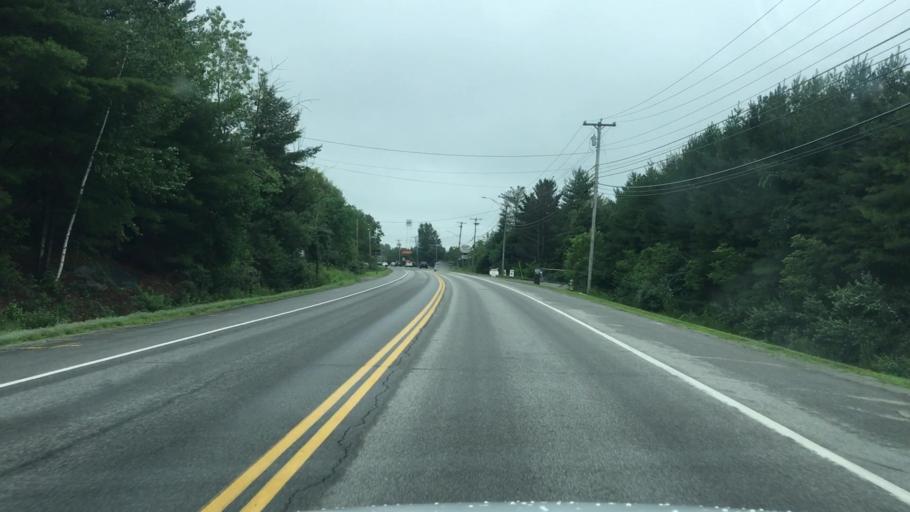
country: US
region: Maine
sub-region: Kennebec County
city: Augusta
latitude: 44.3539
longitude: -69.7973
